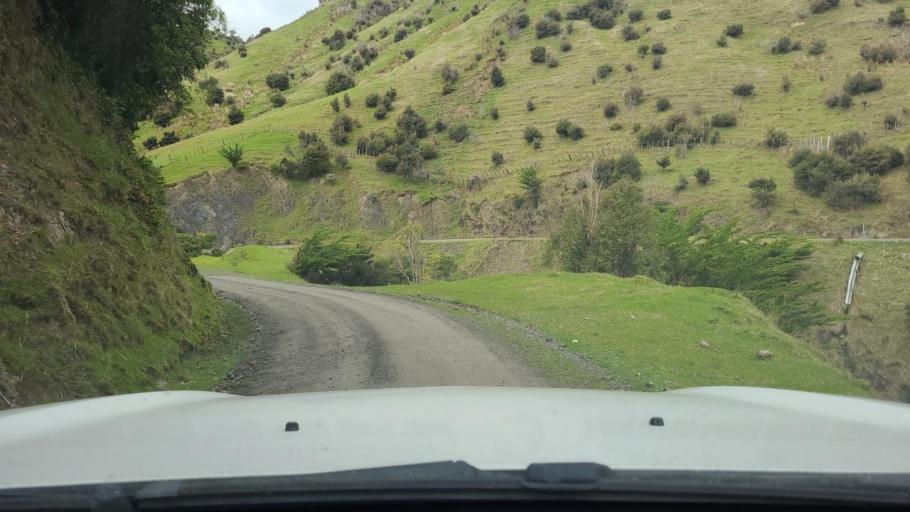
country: NZ
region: Wellington
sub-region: South Wairarapa District
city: Waipawa
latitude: -41.3661
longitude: 175.3936
